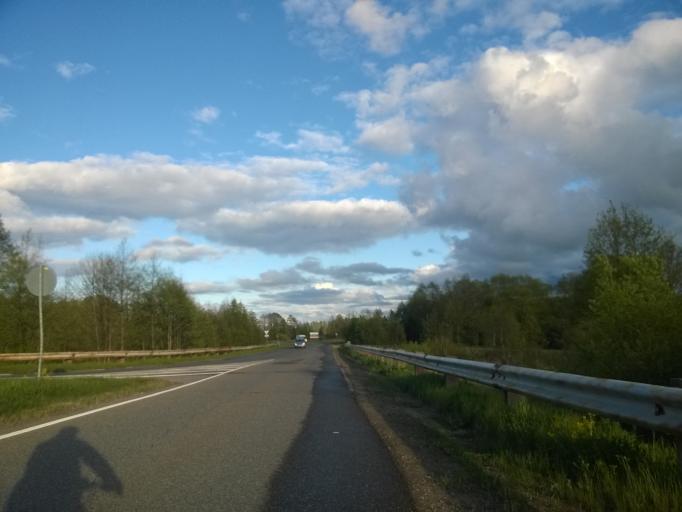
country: LV
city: Tireli
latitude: 56.9319
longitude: 23.6013
